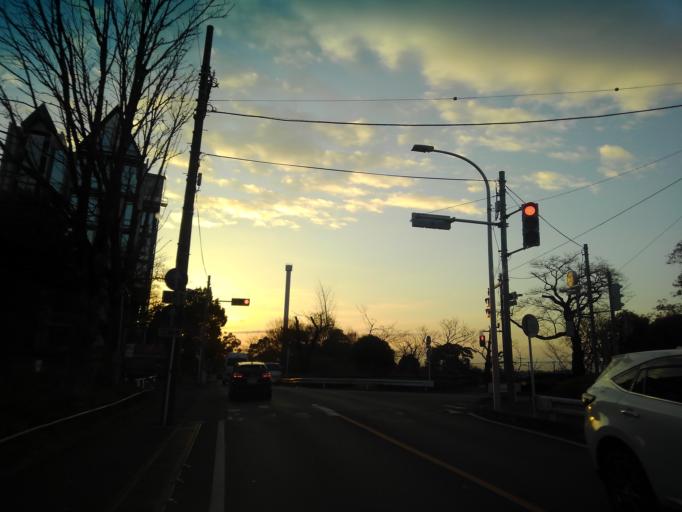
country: JP
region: Tokyo
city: Higashimurayama-shi
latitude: 35.7696
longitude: 139.4384
